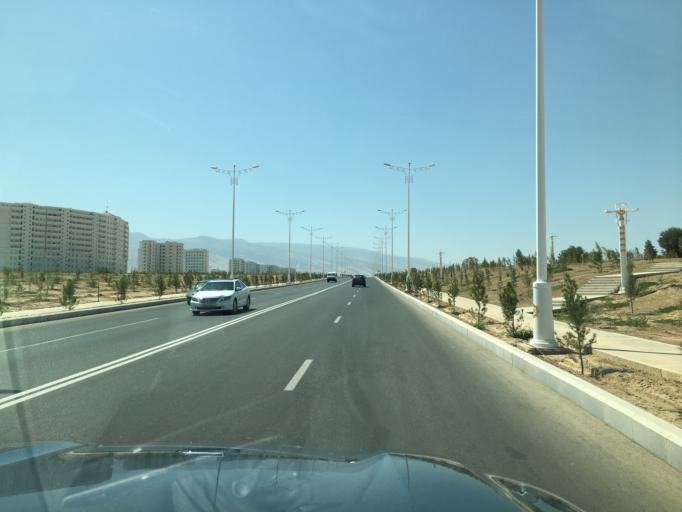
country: TM
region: Ahal
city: Ashgabat
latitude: 37.9274
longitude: 58.3659
